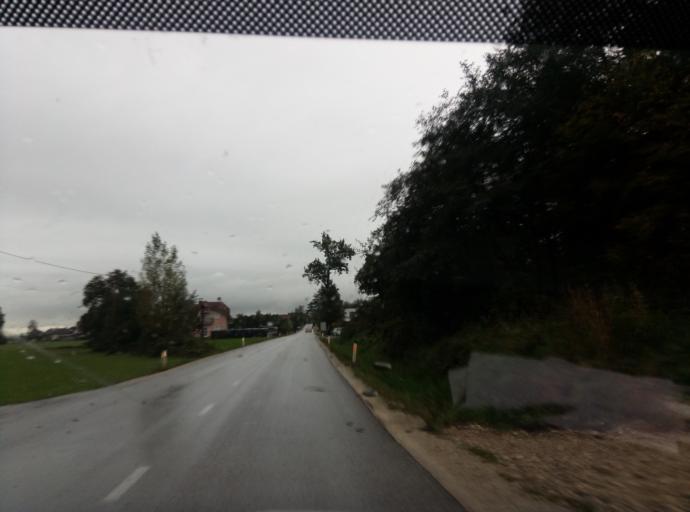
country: SI
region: Medvode
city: Zgornje Pirnice
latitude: 46.1320
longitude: 14.4779
